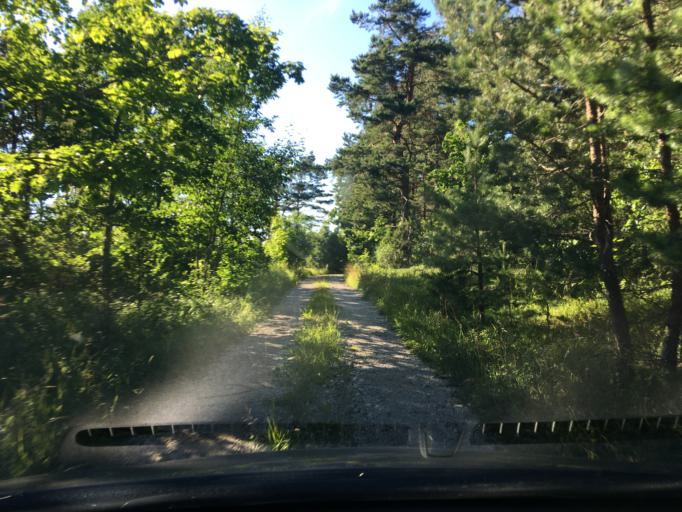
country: EE
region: Laeaene
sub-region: Lihula vald
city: Lihula
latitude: 58.5877
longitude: 23.7441
